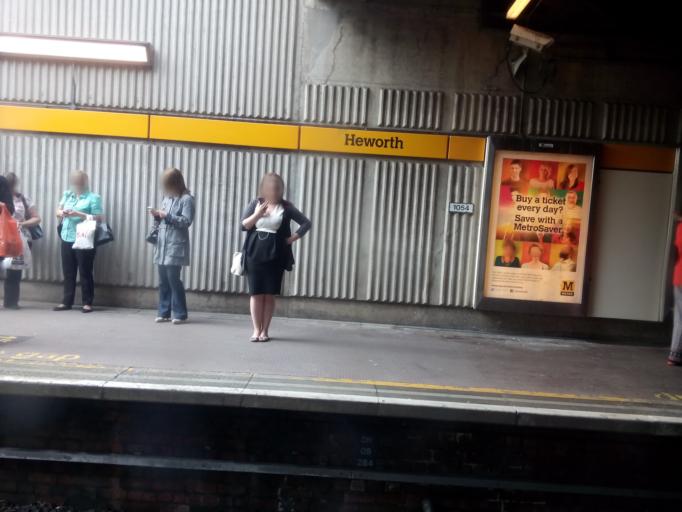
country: GB
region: England
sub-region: Gateshead
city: Felling
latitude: 54.9515
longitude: -1.5568
